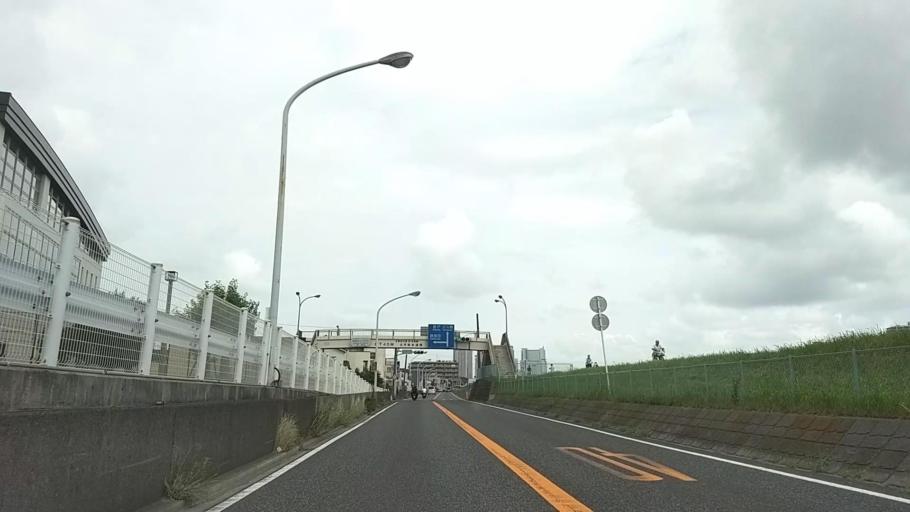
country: JP
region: Kanagawa
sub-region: Kawasaki-shi
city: Kawasaki
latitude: 35.5557
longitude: 139.6861
